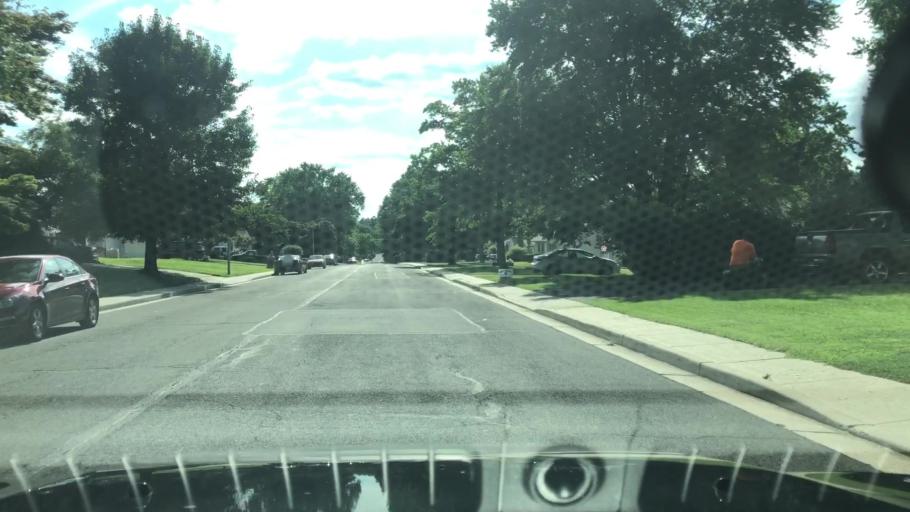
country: US
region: Pennsylvania
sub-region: Bucks County
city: Fairless Hills
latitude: 40.1836
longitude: -74.8434
